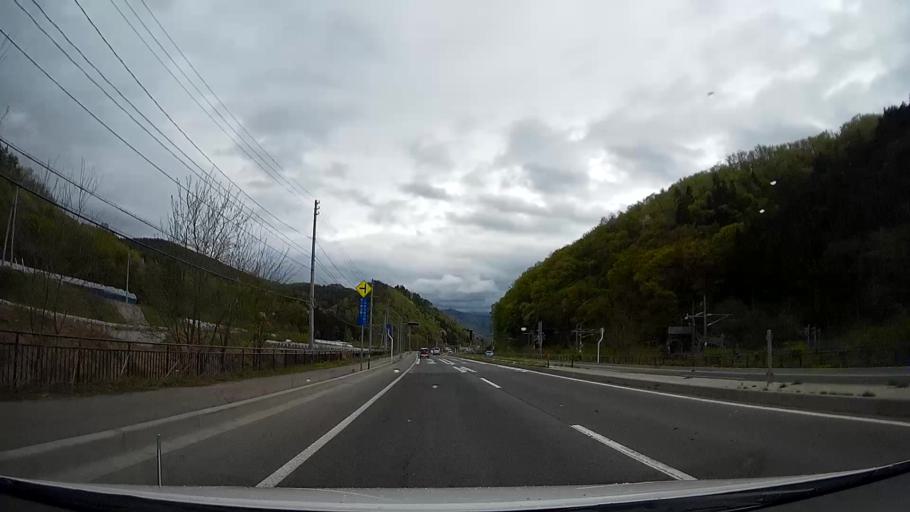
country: JP
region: Yamagata
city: Kaminoyama
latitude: 38.1301
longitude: 140.2242
